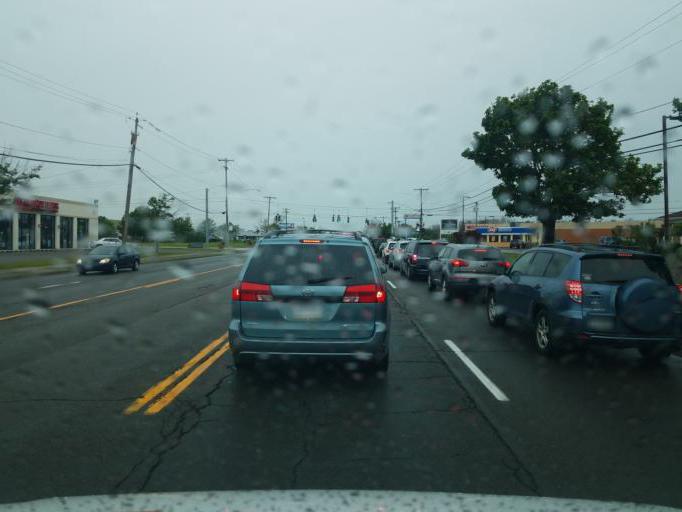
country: US
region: New York
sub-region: Niagara County
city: Niagara Falls
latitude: 43.1002
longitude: -78.9778
